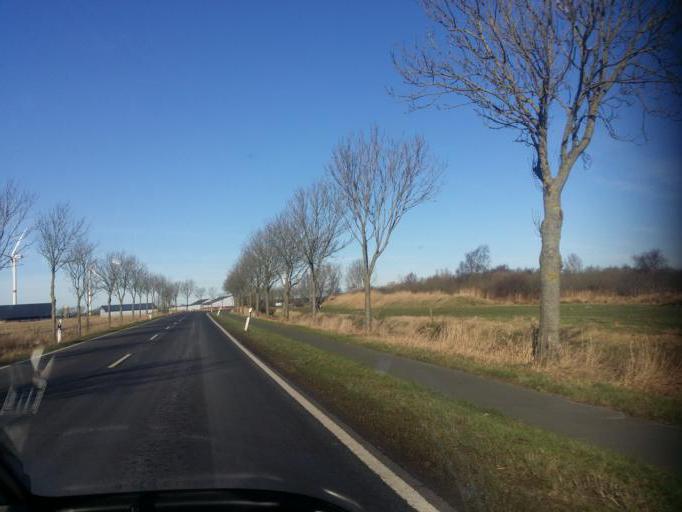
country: DE
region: Schleswig-Holstein
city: Husum
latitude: 54.4533
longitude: 9.0445
